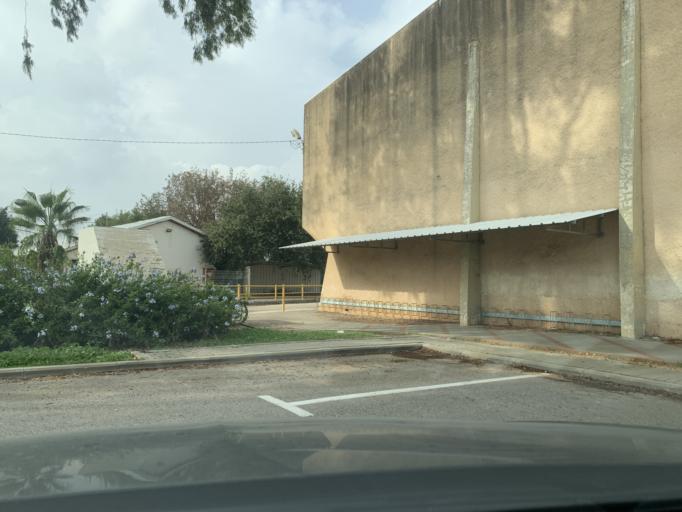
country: IL
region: Central District
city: Tirah
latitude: 32.2158
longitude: 34.9381
